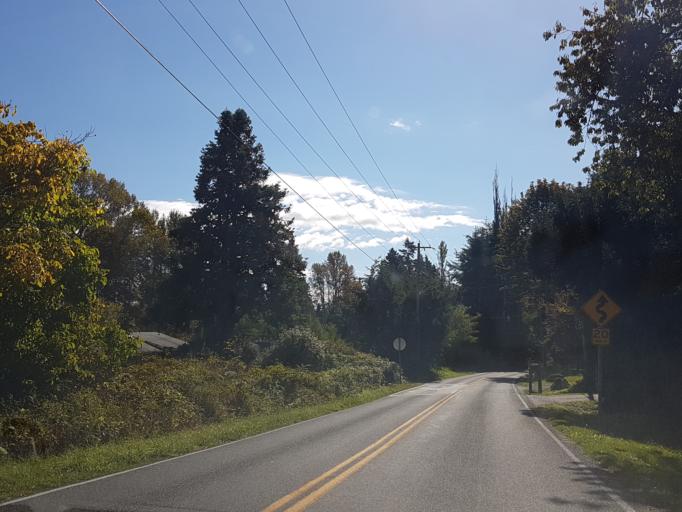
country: US
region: Washington
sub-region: Snohomish County
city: Cathcart
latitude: 47.8469
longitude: -122.0986
